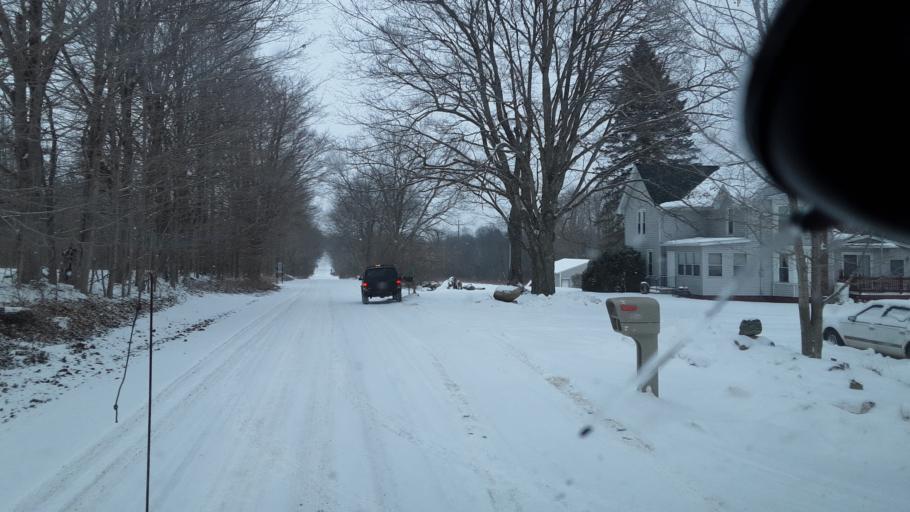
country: US
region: Michigan
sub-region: Ingham County
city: Leslie
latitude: 42.4221
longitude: -84.4767
